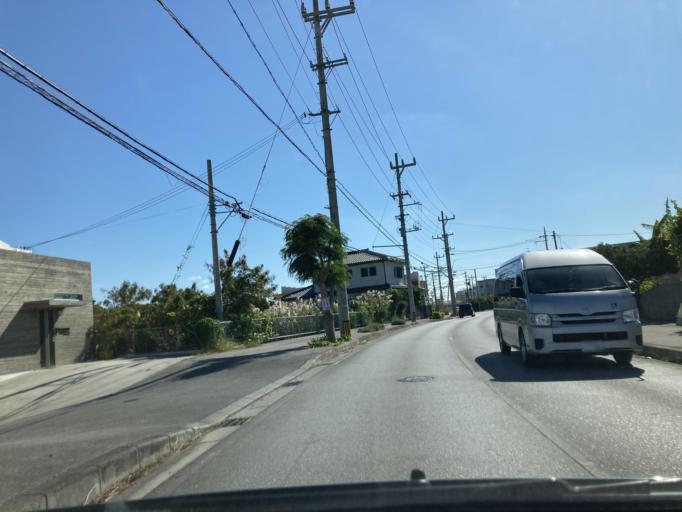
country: JP
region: Okinawa
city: Okinawa
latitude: 26.3611
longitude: 127.8251
